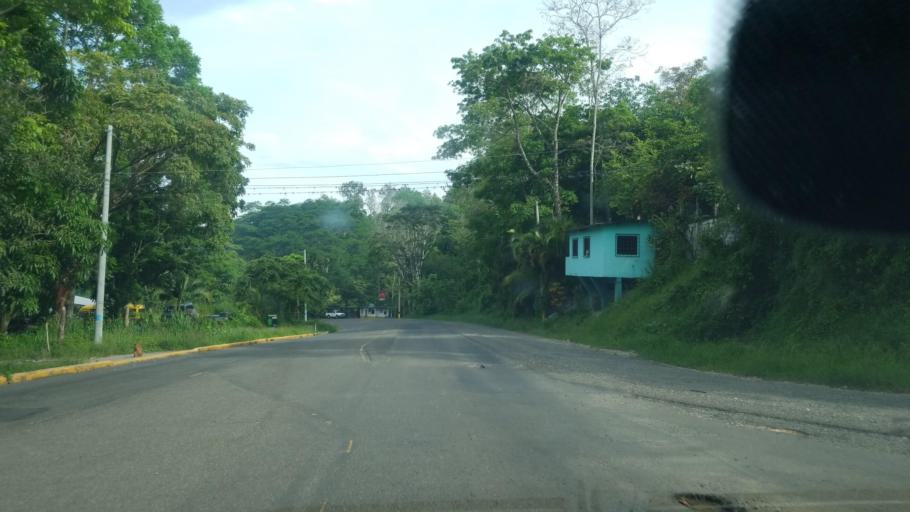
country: HN
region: Santa Barbara
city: Trinidad
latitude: 15.1826
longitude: -88.2752
